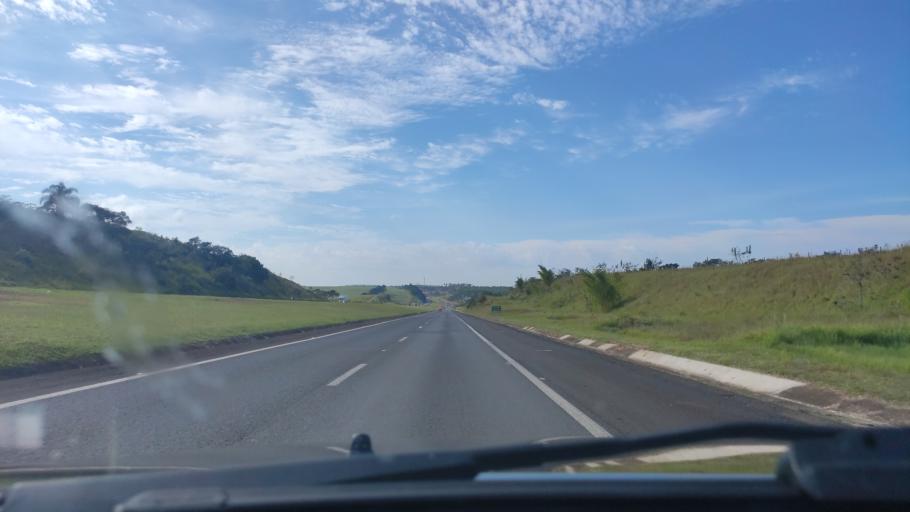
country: BR
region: Sao Paulo
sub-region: Itatinga
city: Itatinga
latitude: -23.1246
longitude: -48.4787
